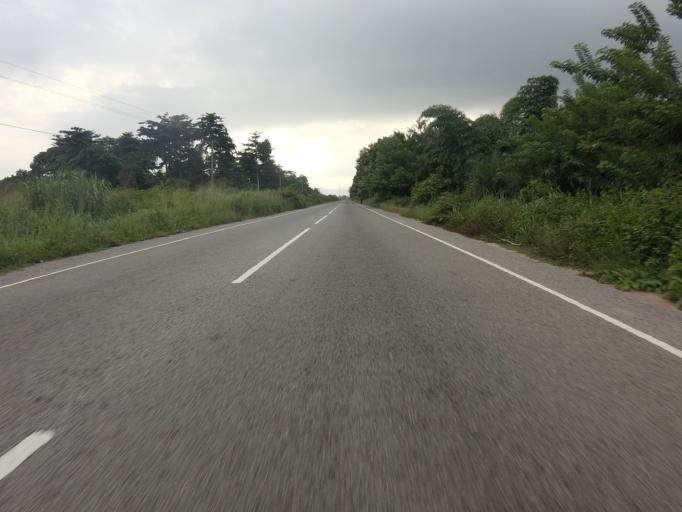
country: GH
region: Volta
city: Ho
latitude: 6.7775
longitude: 0.4720
